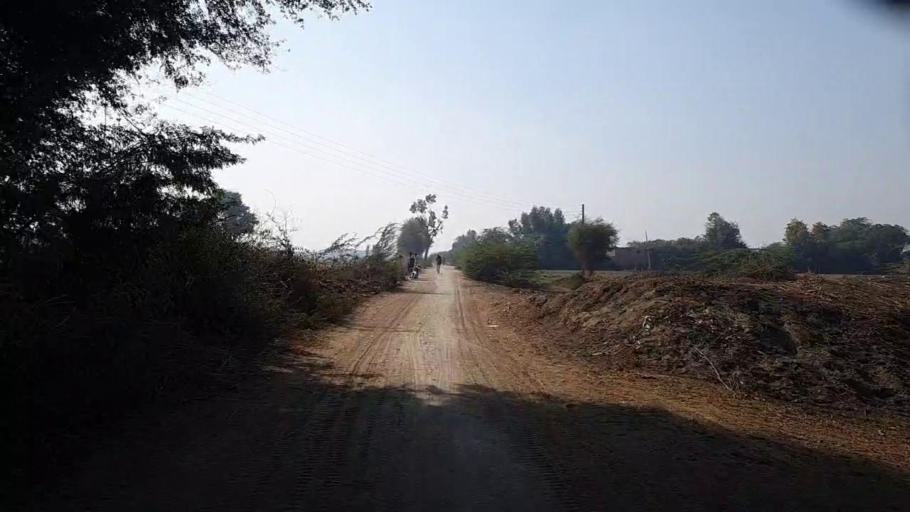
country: PK
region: Sindh
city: Bozdar
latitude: 27.2432
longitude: 68.6037
